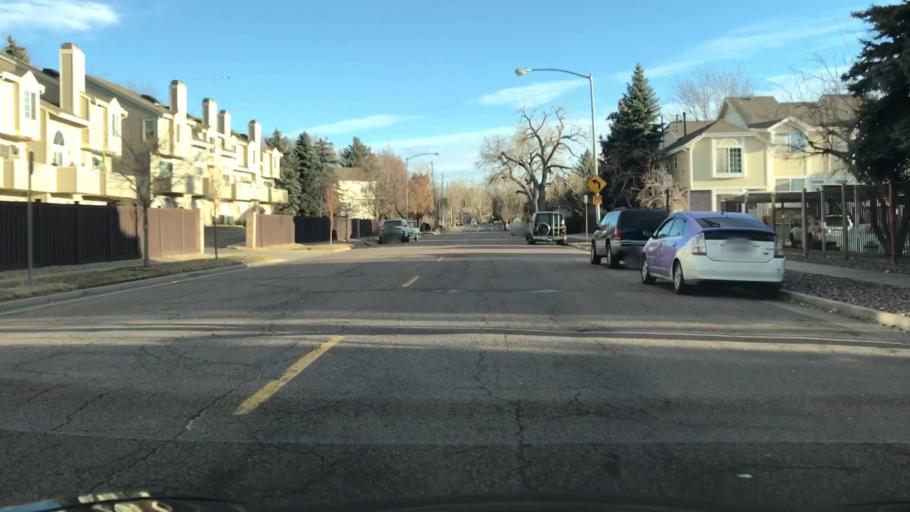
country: US
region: Colorado
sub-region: Arapahoe County
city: Glendale
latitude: 39.6837
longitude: -104.8909
